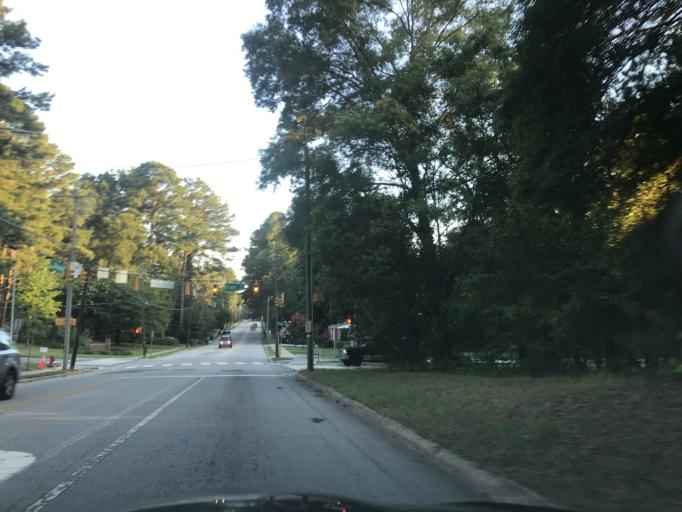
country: US
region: North Carolina
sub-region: Wake County
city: Raleigh
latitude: 35.7965
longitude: -78.6243
